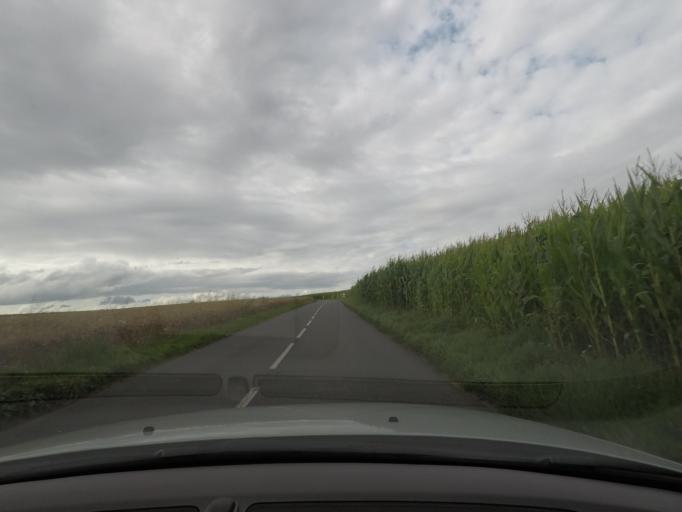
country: FR
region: Haute-Normandie
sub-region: Departement de la Seine-Maritime
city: Ymare
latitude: 49.3387
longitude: 1.1908
